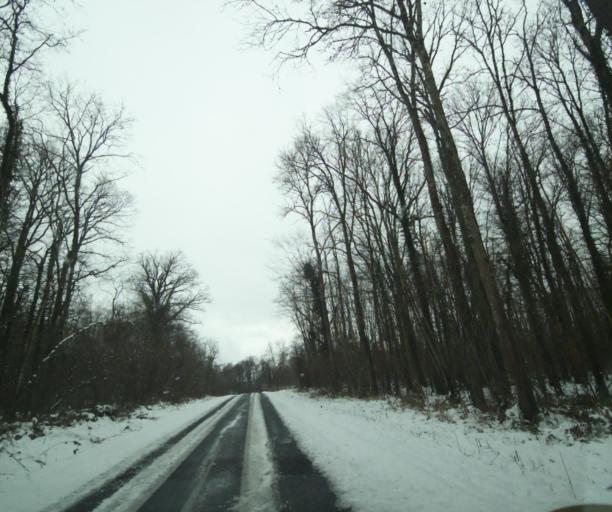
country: FR
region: Champagne-Ardenne
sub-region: Departement de la Haute-Marne
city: Montier-en-Der
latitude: 48.4229
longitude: 4.7283
